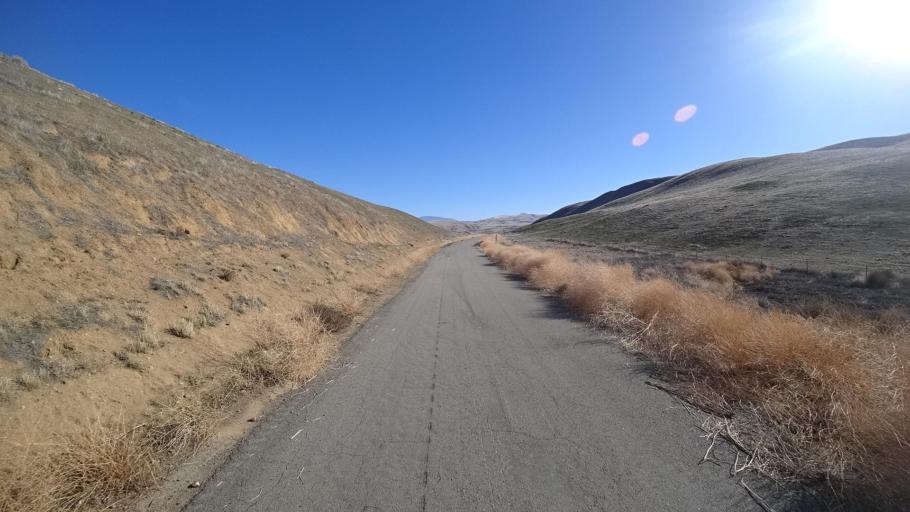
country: US
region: California
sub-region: Kern County
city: Maricopa
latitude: 34.9817
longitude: -119.4690
